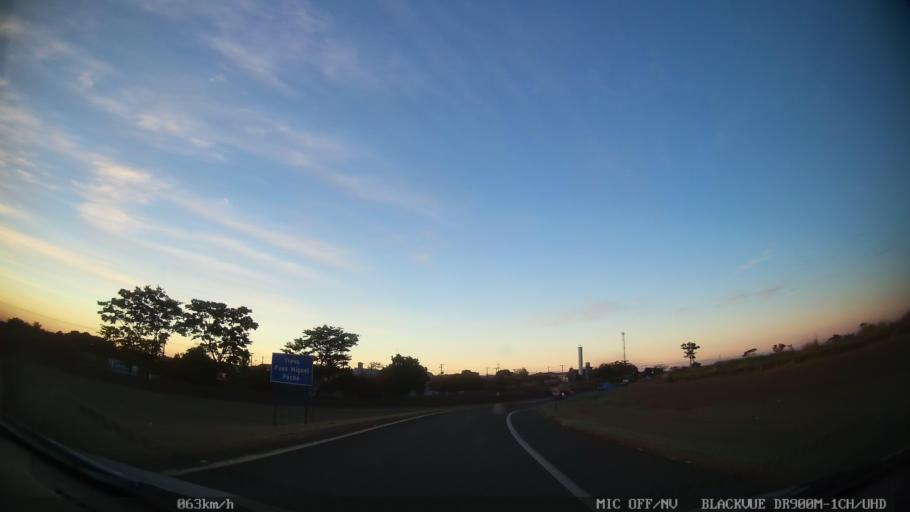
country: BR
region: Sao Paulo
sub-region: Catanduva
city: Catanduva
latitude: -21.1329
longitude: -49.0180
